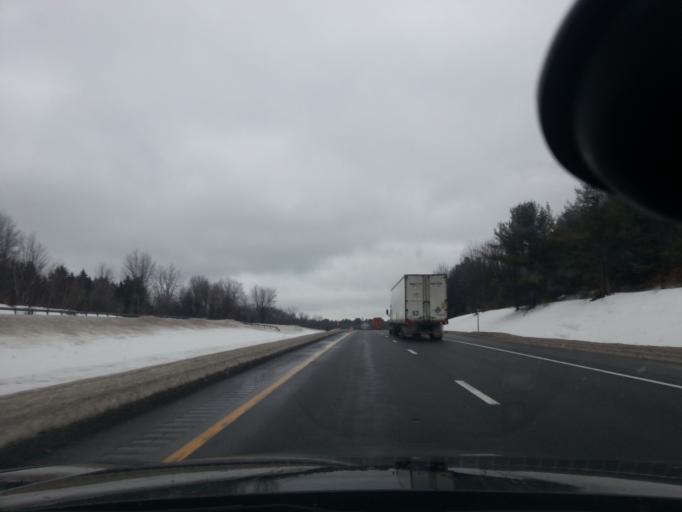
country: US
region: New York
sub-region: Oswego County
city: Central Square
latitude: 43.3697
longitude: -76.1218
